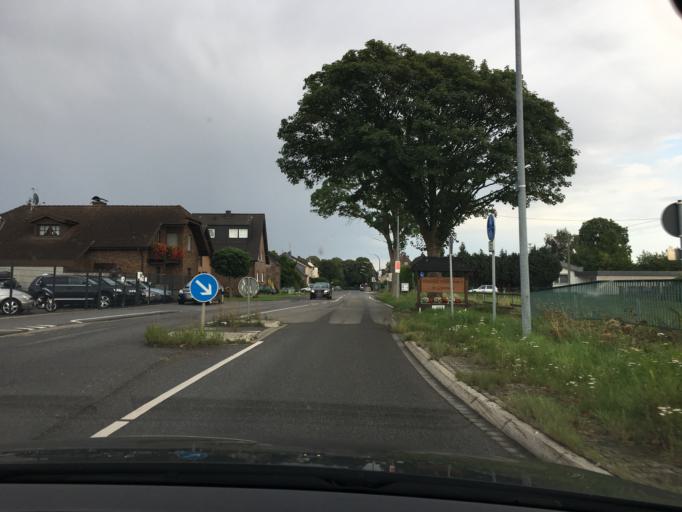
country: DE
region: North Rhine-Westphalia
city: Tuernich
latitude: 50.8419
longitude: 6.7332
